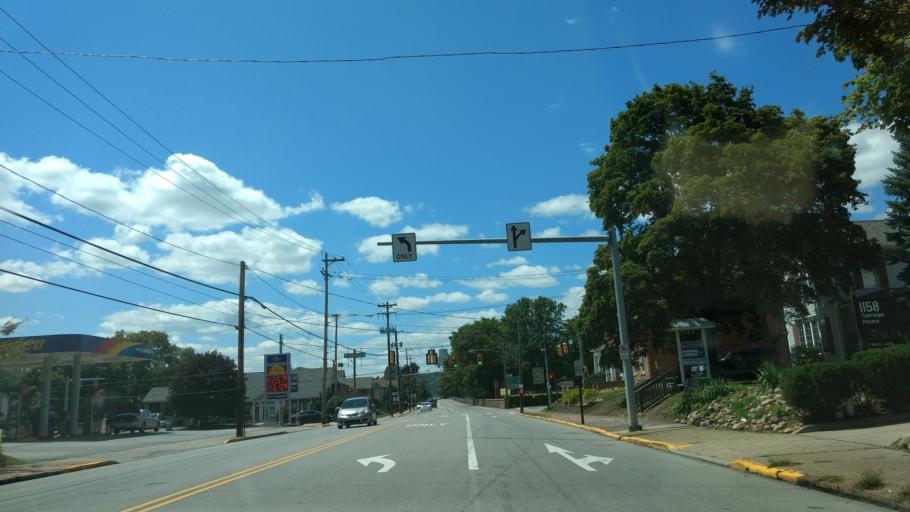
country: US
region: Pennsylvania
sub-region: Beaver County
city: Beaver
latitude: 40.6924
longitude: -80.3119
